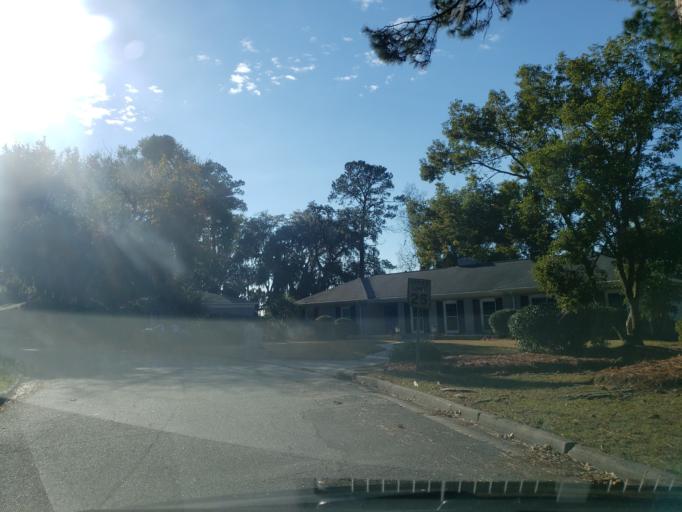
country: US
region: Georgia
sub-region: Chatham County
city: Thunderbolt
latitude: 32.0630
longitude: -81.0334
